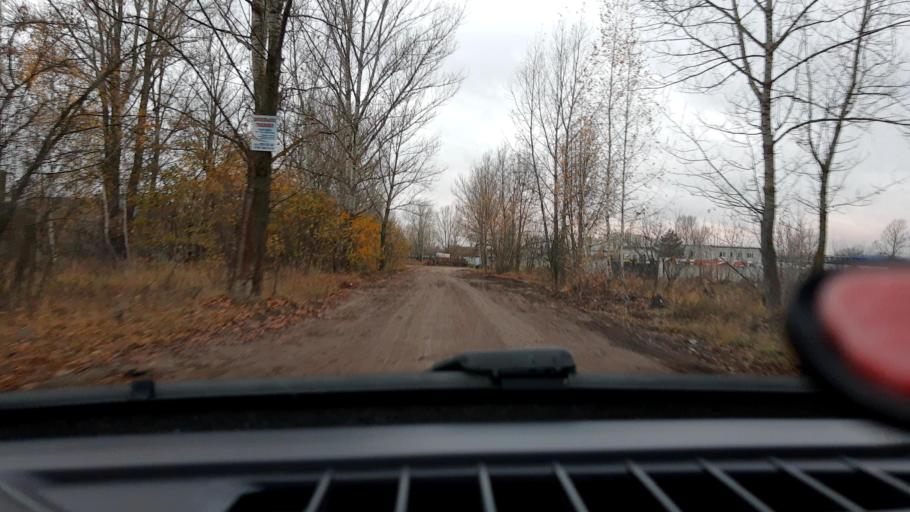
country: RU
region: Nizjnij Novgorod
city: Neklyudovo
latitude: 56.3552
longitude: 43.8903
